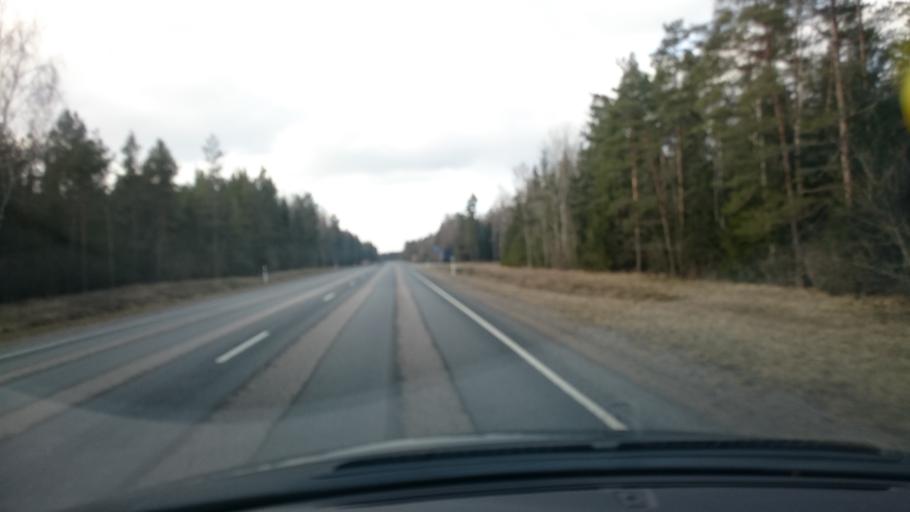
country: EE
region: Harju
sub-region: Nissi vald
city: Turba
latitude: 58.9586
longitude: 24.0755
